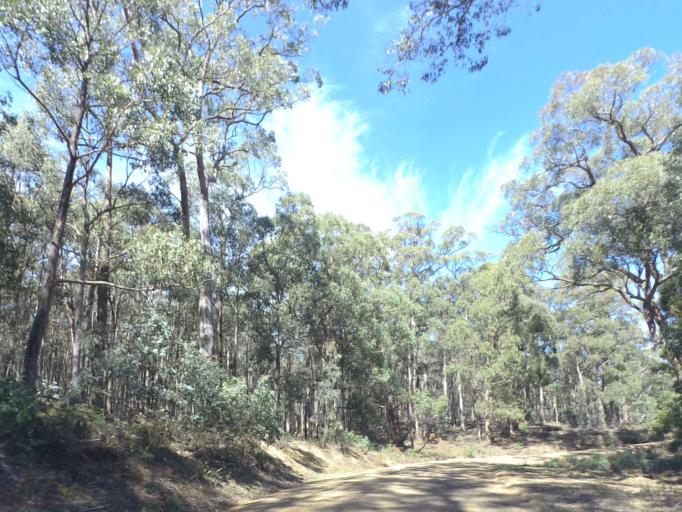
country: AU
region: Victoria
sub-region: Moorabool
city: Bacchus Marsh
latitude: -37.4366
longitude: 144.3629
